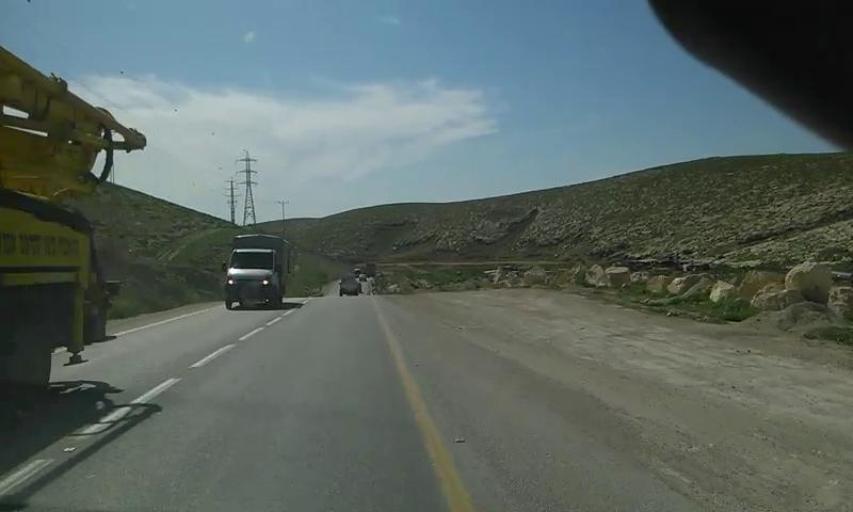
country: PS
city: Az Za`ayyim
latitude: 31.8095
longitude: 35.3068
